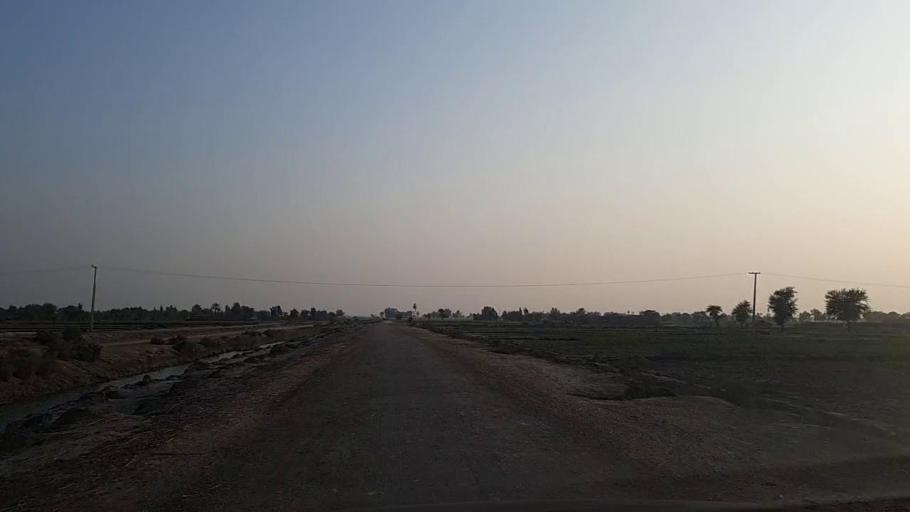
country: PK
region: Sindh
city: Daur
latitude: 26.4179
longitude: 68.3884
